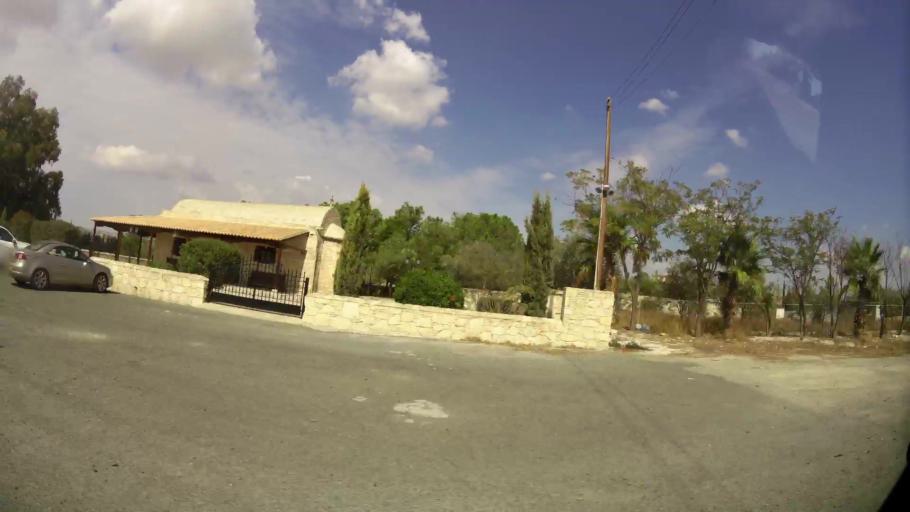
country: CY
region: Larnaka
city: Aradippou
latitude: 34.9613
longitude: 33.5658
